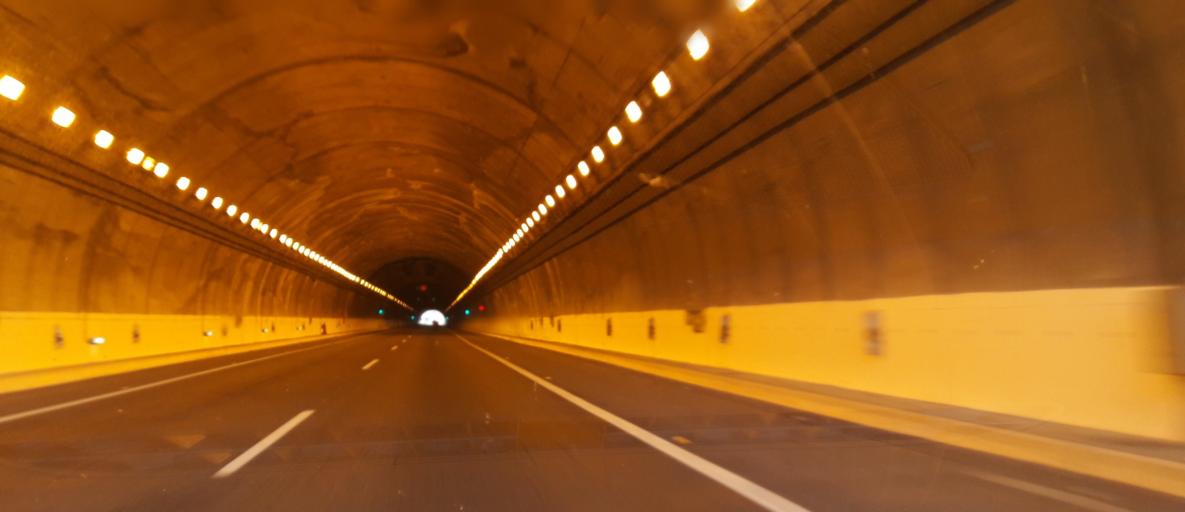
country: ES
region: Andalusia
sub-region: Provincia de Almeria
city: Aguadulce
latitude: 36.8209
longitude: -2.5635
